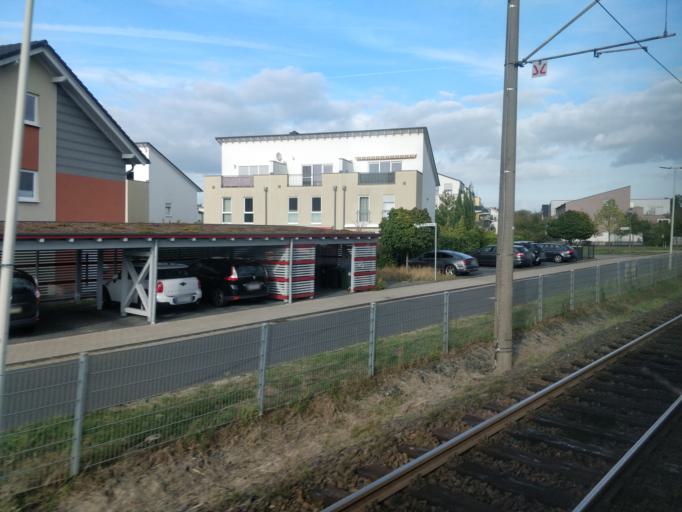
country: DE
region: North Rhine-Westphalia
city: Sankt Augustin
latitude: 50.7549
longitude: 7.1501
